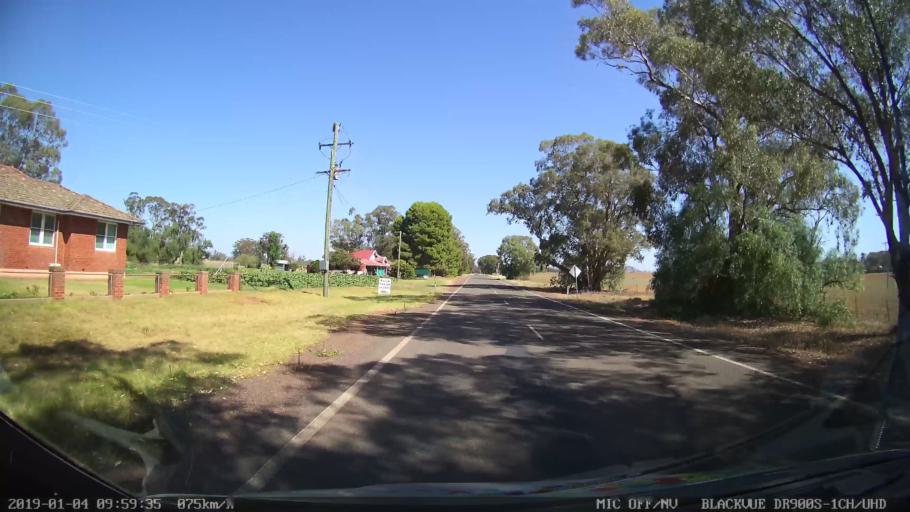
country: AU
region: New South Wales
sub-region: Cabonne
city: Canowindra
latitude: -33.5061
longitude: 148.3852
